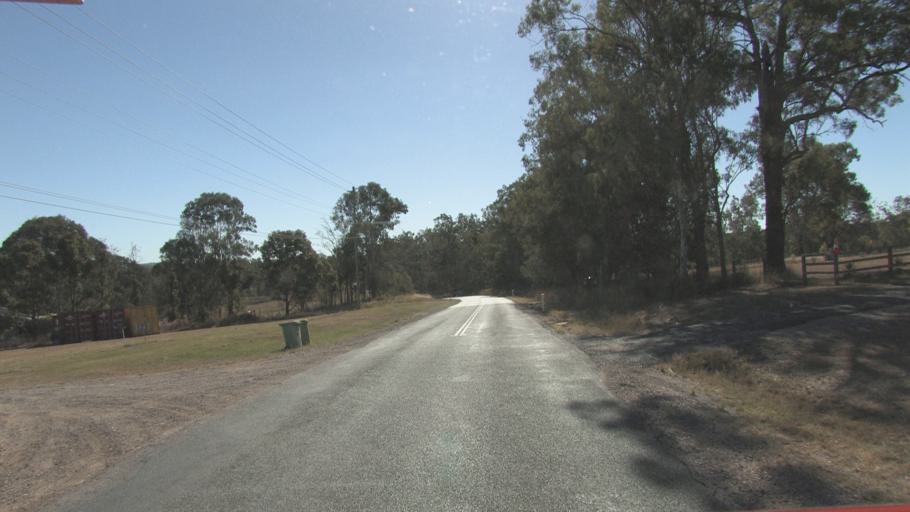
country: AU
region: Queensland
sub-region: Logan
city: North Maclean
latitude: -27.7685
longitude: 153.0018
